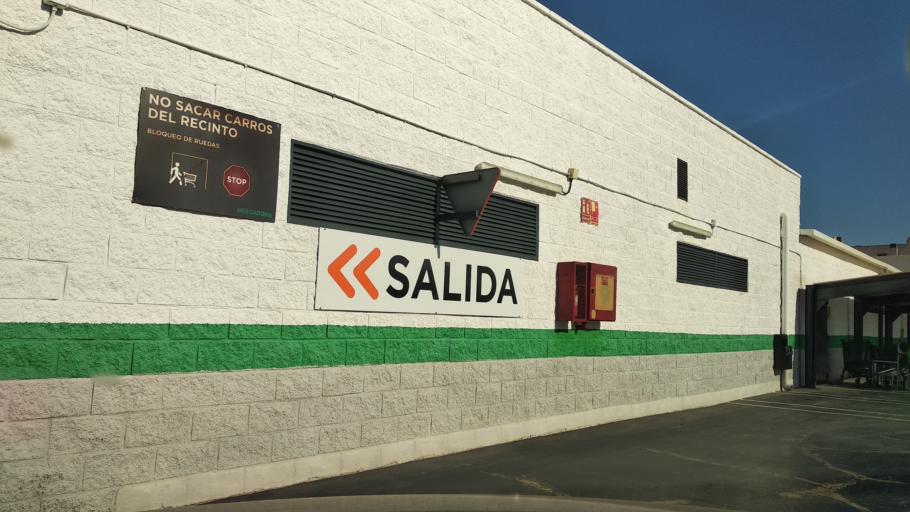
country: ES
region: Murcia
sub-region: Murcia
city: Santomera
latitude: 38.0642
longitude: -1.0522
